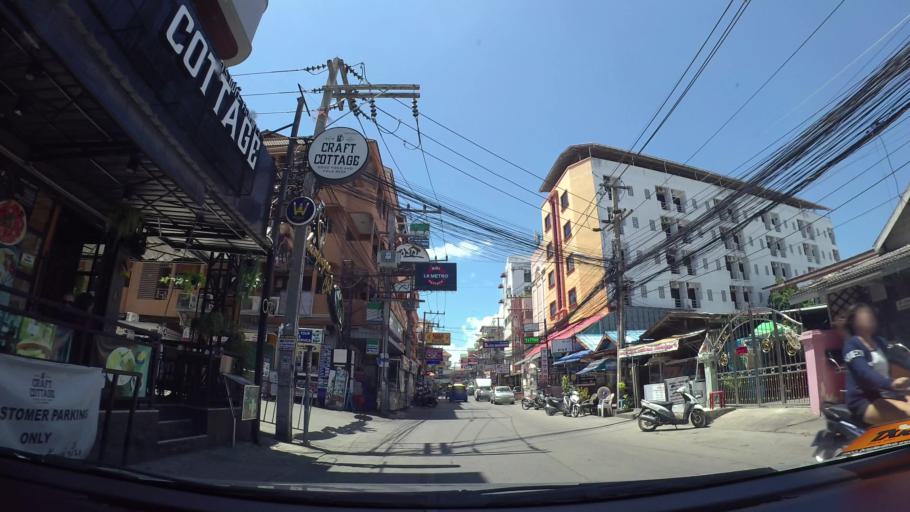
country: TH
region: Chon Buri
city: Phatthaya
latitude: 12.9295
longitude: 100.8838
